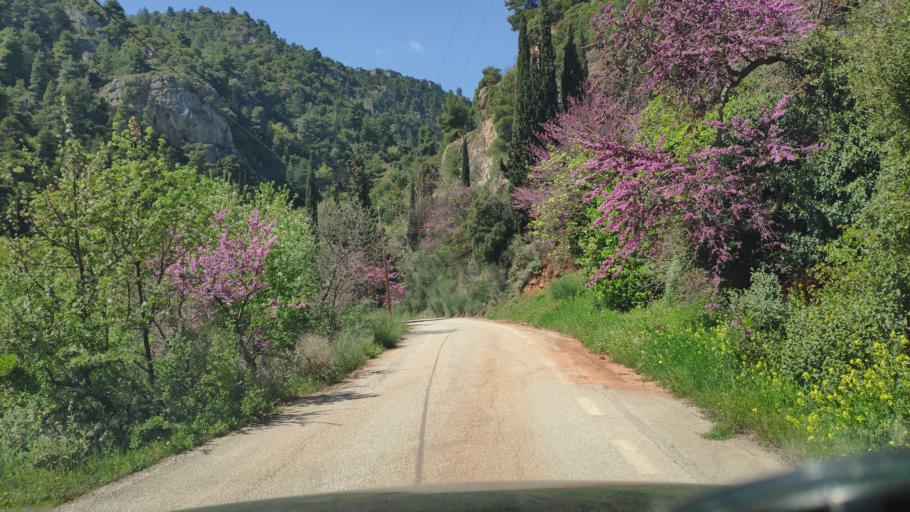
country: GR
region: West Greece
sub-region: Nomos Achaias
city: Akrata
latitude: 38.0963
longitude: 22.3181
